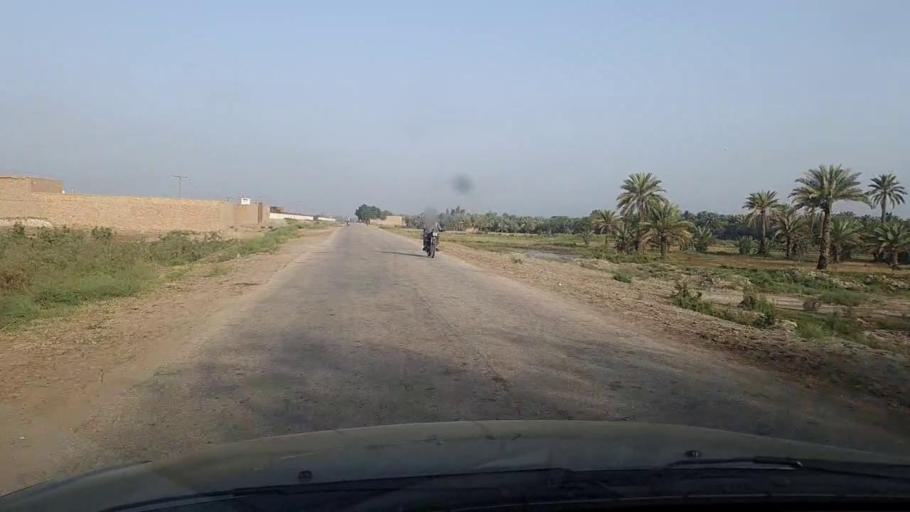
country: PK
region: Sindh
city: Khairpur
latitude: 27.5464
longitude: 68.6998
